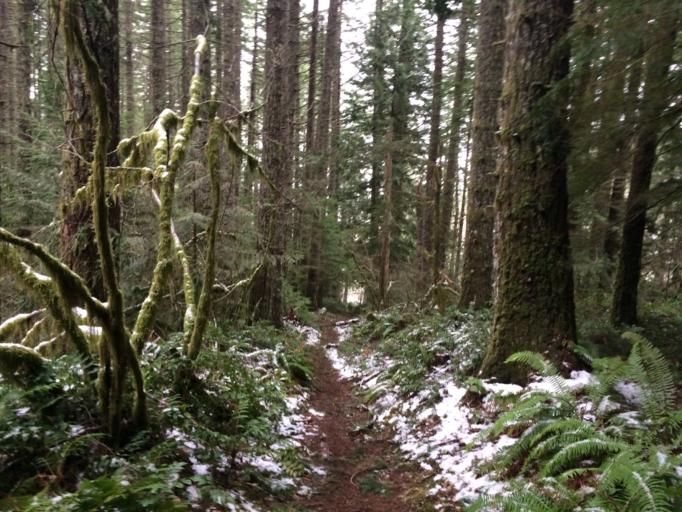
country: US
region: Oregon
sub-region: Benton County
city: Philomath
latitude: 44.5300
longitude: -123.5468
